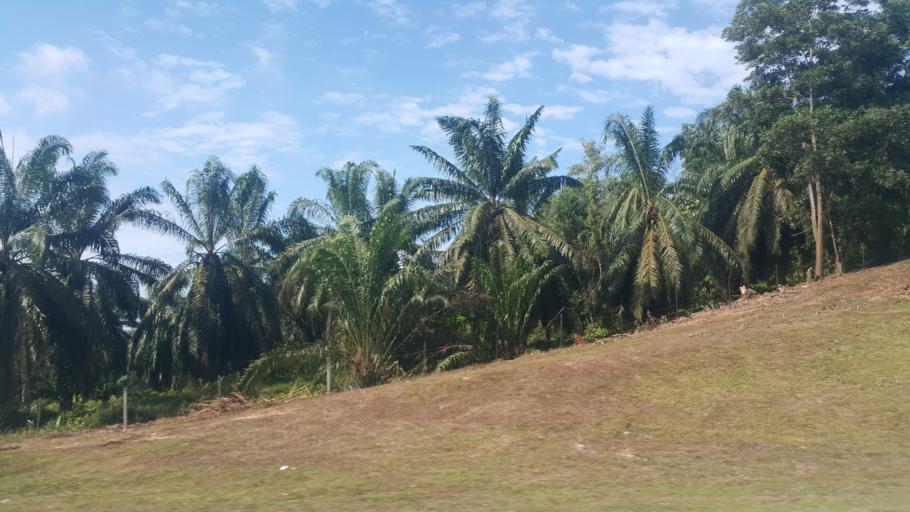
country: MY
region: Johor
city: Kelapa Sawit
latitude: 1.7223
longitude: 103.4319
